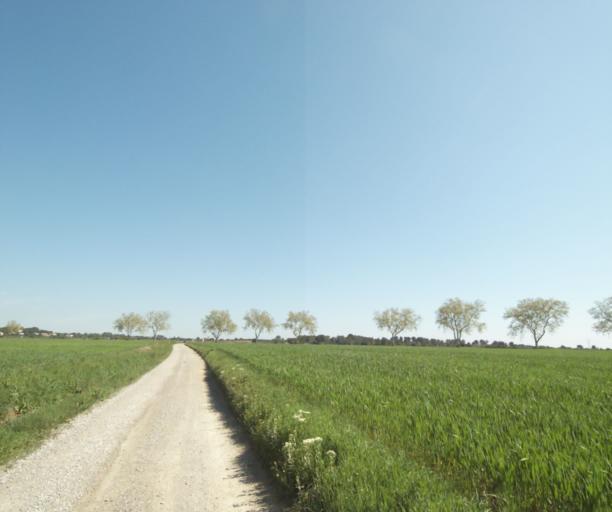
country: FR
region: Languedoc-Roussillon
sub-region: Departement de l'Herault
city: Saint-Bres
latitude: 43.6787
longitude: 4.0221
